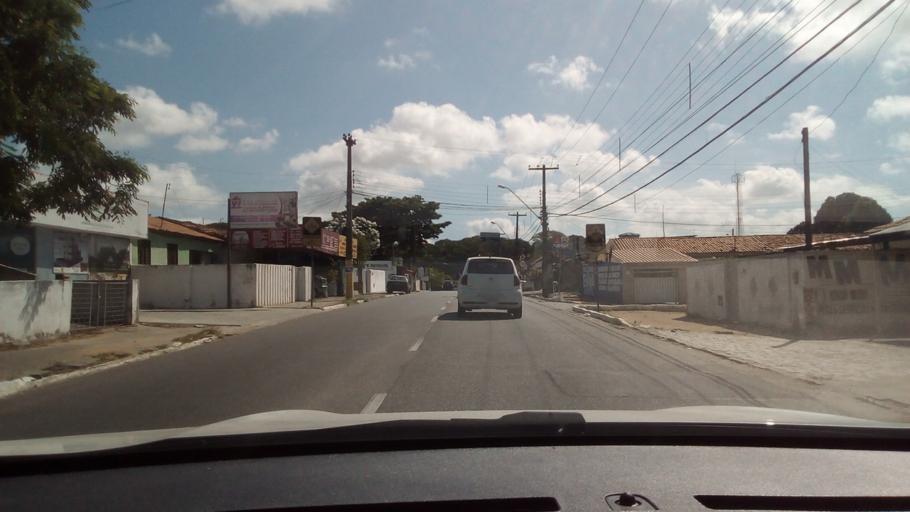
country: BR
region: Paraiba
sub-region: Joao Pessoa
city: Joao Pessoa
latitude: -7.1307
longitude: -34.8451
